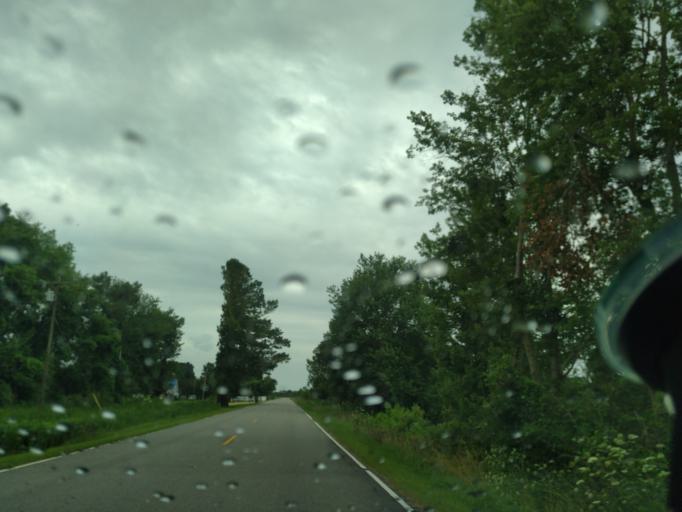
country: US
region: North Carolina
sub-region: Beaufort County
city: Belhaven
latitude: 35.7600
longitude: -76.5197
